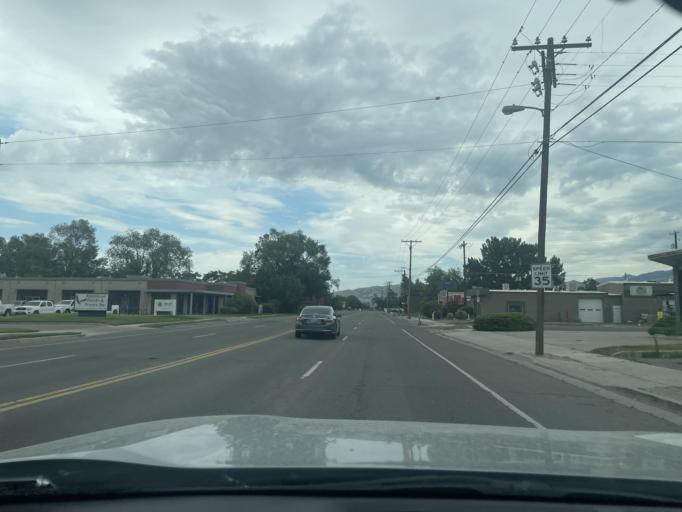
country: US
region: Utah
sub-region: Salt Lake County
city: South Salt Lake
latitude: 40.7051
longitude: -111.8911
